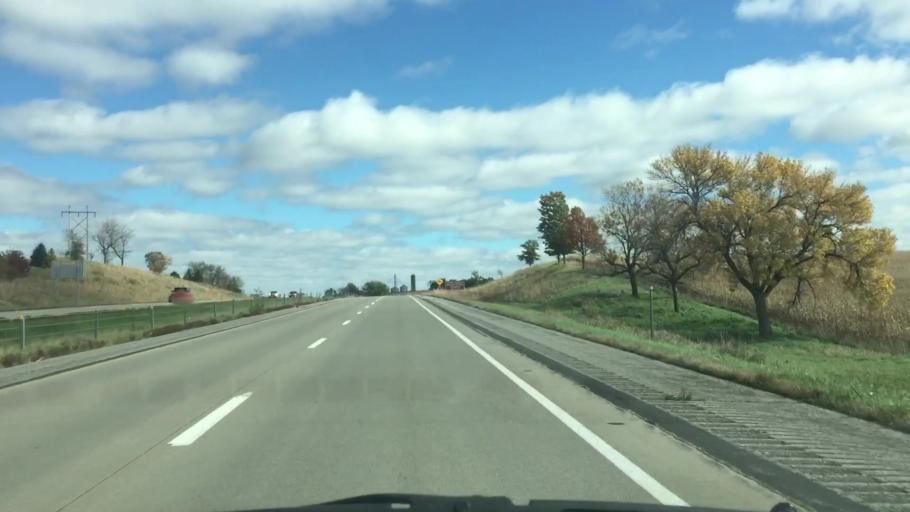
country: US
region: Iowa
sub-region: Iowa County
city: Williamsburg
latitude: 41.6874
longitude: -92.0519
